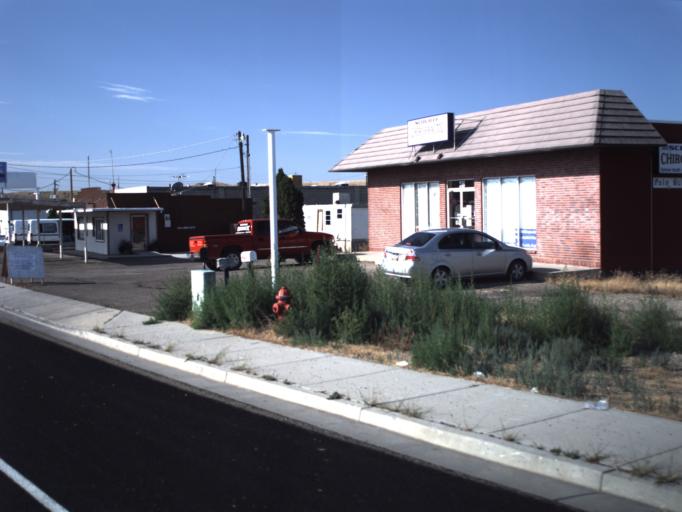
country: US
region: Utah
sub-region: Carbon County
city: Price
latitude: 39.5961
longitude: -110.7912
